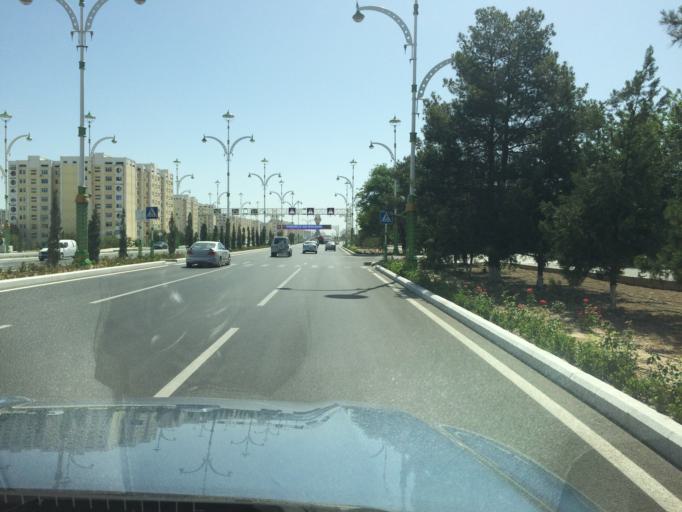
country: TM
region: Ahal
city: Ashgabat
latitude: 37.8955
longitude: 58.3824
